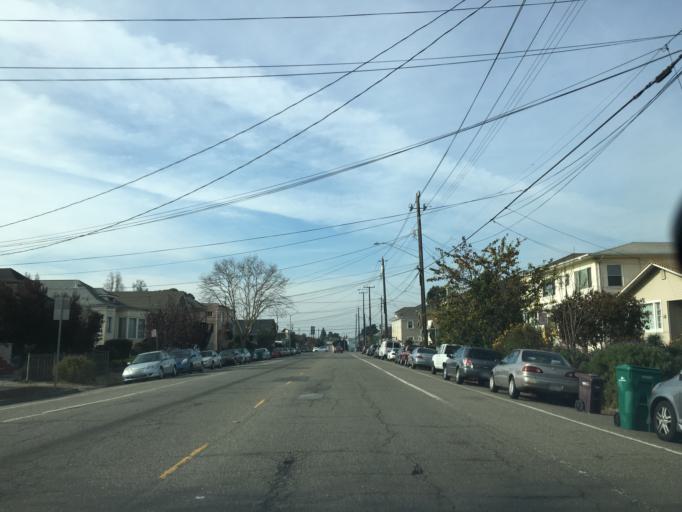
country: US
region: California
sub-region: Alameda County
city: Emeryville
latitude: 37.8395
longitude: -122.2721
